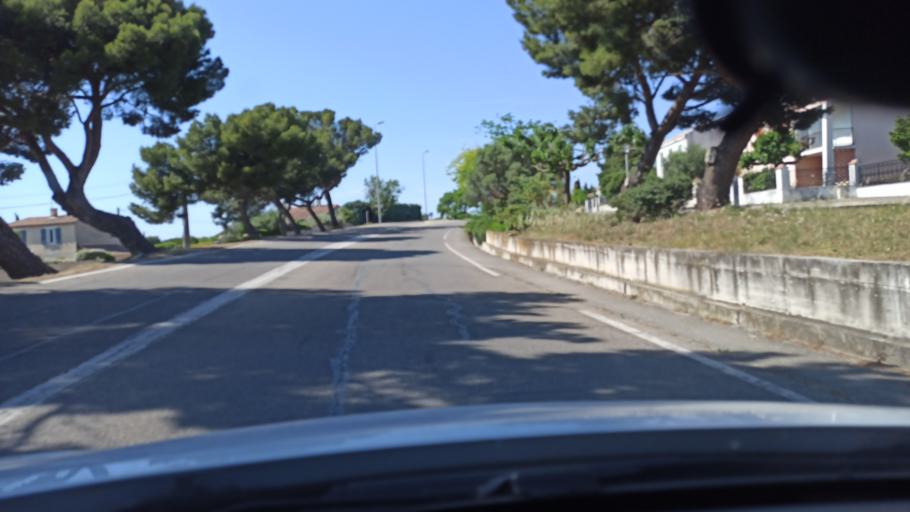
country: FR
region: Provence-Alpes-Cote d'Azur
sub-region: Departement des Bouches-du-Rhone
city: Chateaurenard
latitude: 43.8746
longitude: 4.8500
